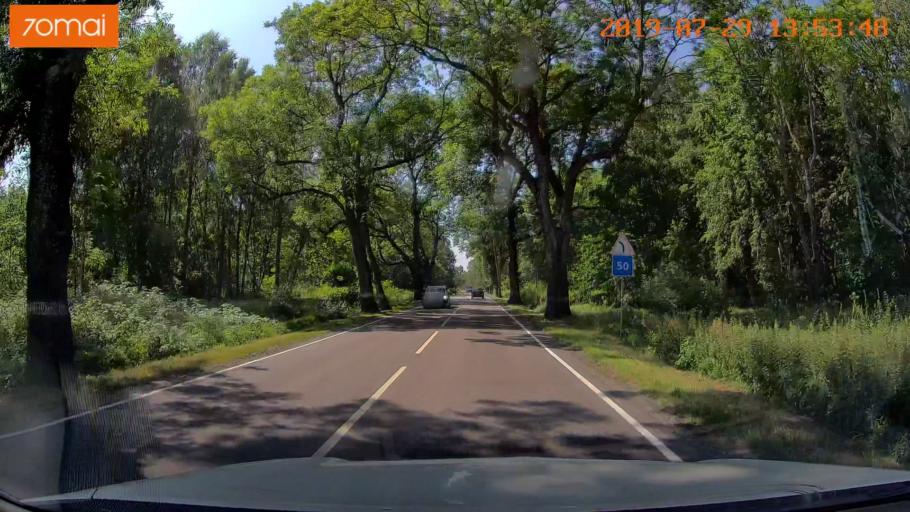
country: RU
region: Kaliningrad
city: Primorsk
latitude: 54.7276
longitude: 19.9744
